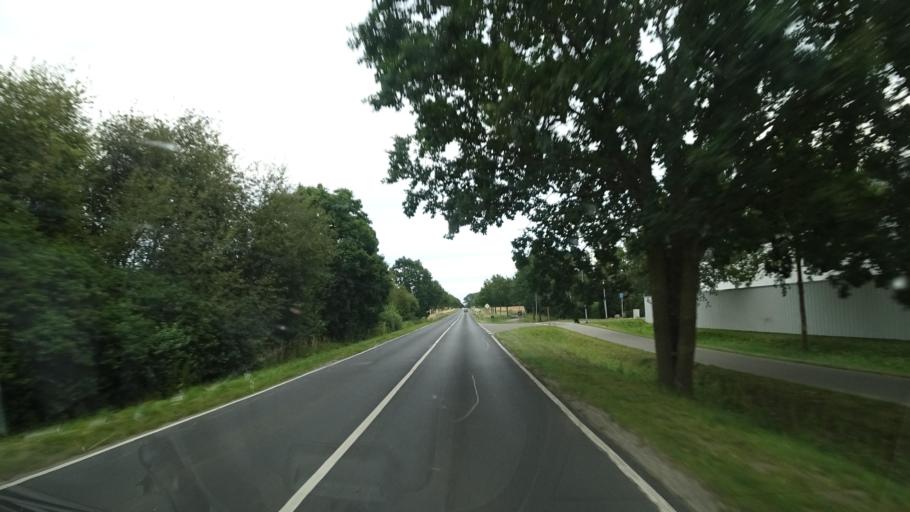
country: DE
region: Mecklenburg-Vorpommern
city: Weitenhagen
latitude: 54.0868
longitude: 13.4594
